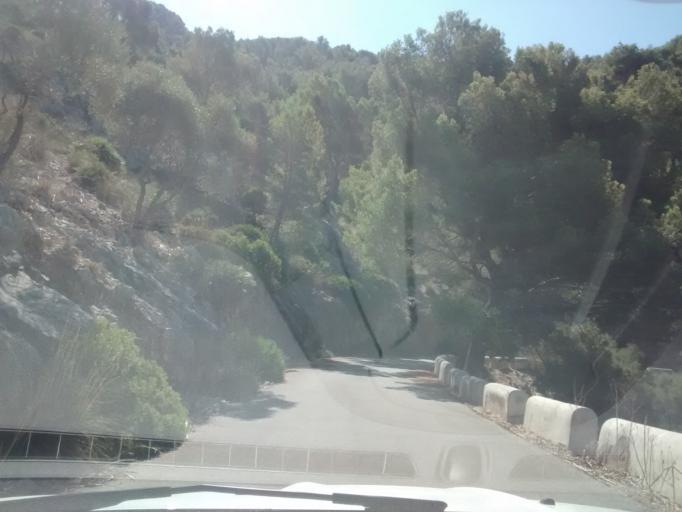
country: ES
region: Balearic Islands
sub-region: Illes Balears
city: Port d'Alcudia
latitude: 39.8757
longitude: 3.1721
